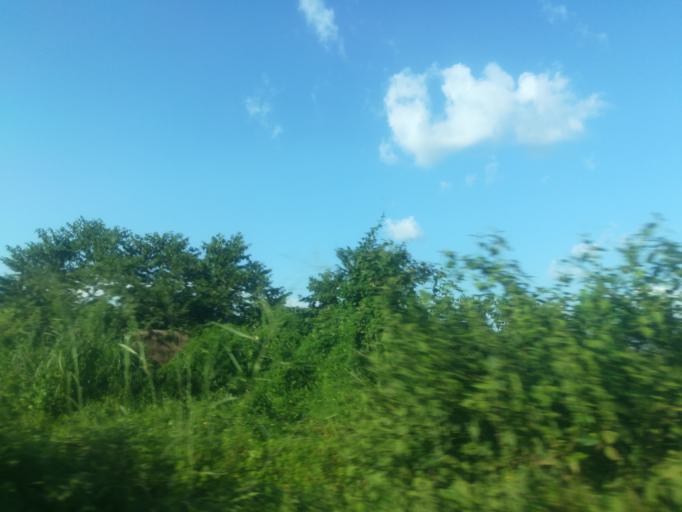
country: NG
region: Oyo
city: Ibadan
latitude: 7.4377
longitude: 3.9673
